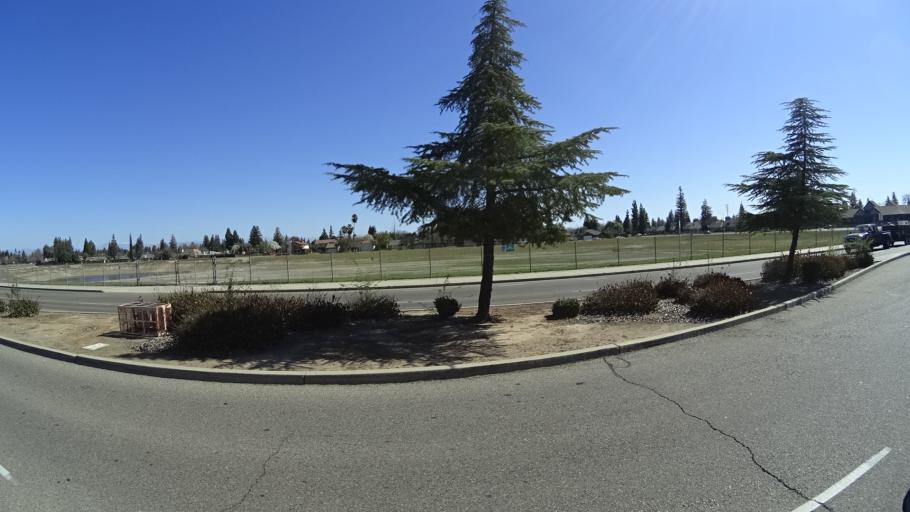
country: US
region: California
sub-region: Fresno County
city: Clovis
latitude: 36.8531
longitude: -119.7842
